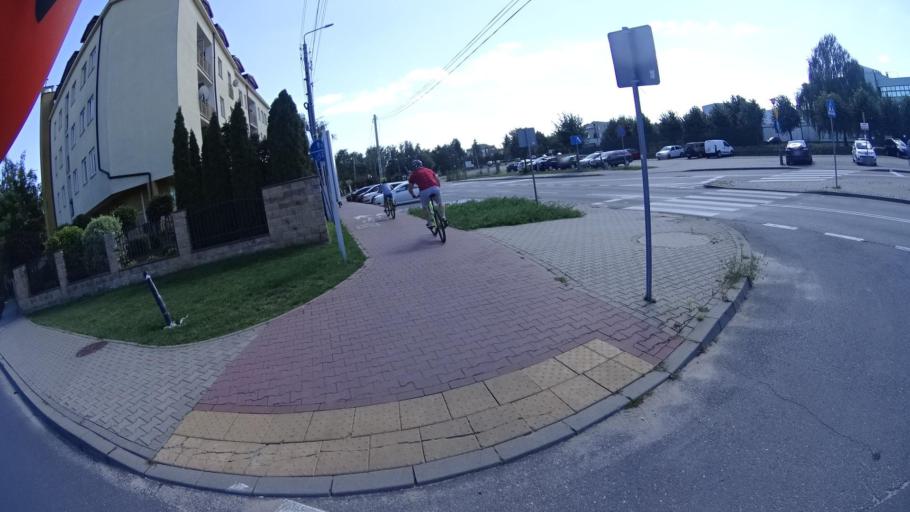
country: PL
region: Masovian Voivodeship
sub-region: Powiat piaseczynski
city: Jozefoslaw
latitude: 52.0986
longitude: 21.0534
